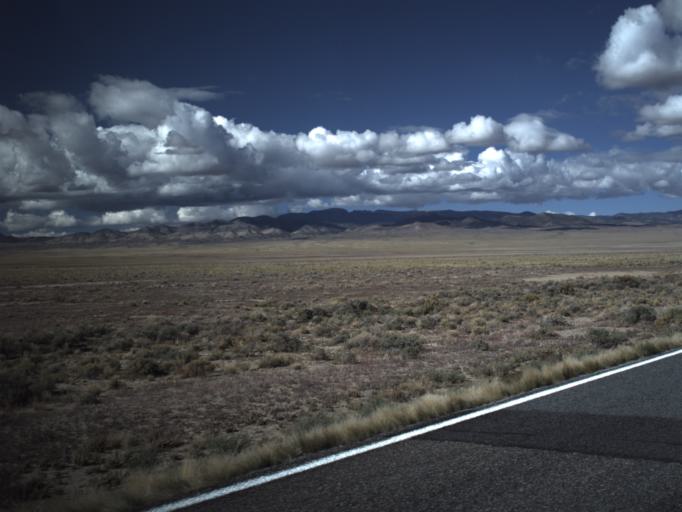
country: US
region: Utah
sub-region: Beaver County
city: Milford
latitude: 38.5362
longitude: -113.6922
